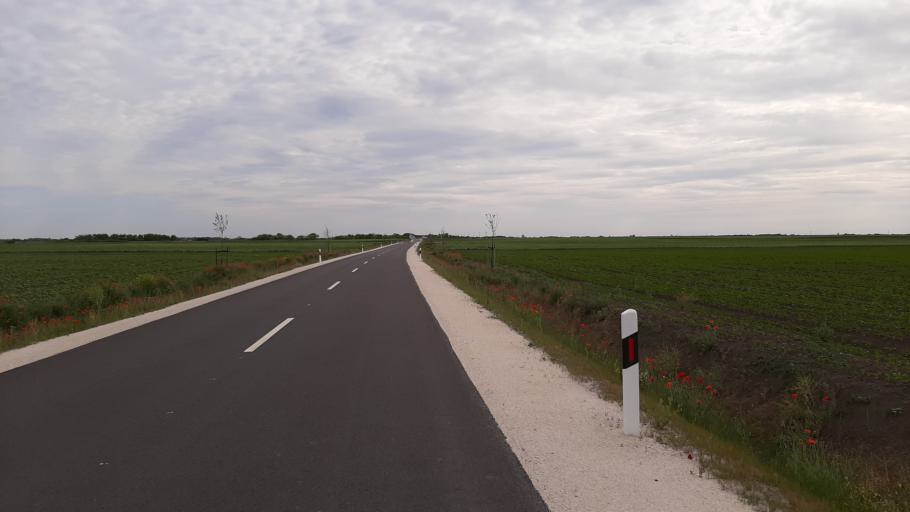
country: RO
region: Timis
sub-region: Comuna Beba Veche
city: Beba Veche
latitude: 46.1323
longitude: 20.2688
